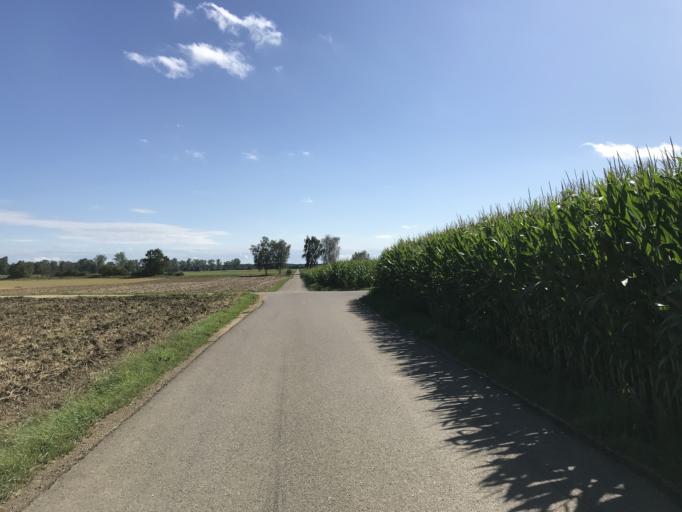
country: DE
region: Baden-Wuerttemberg
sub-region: Tuebingen Region
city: Langenau
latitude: 48.4830
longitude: 10.1242
